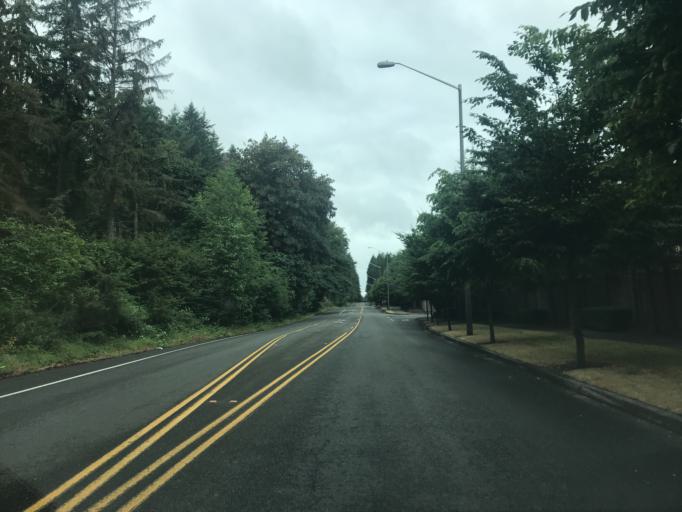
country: US
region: Washington
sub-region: King County
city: Black Diamond
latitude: 47.3435
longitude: -122.0378
